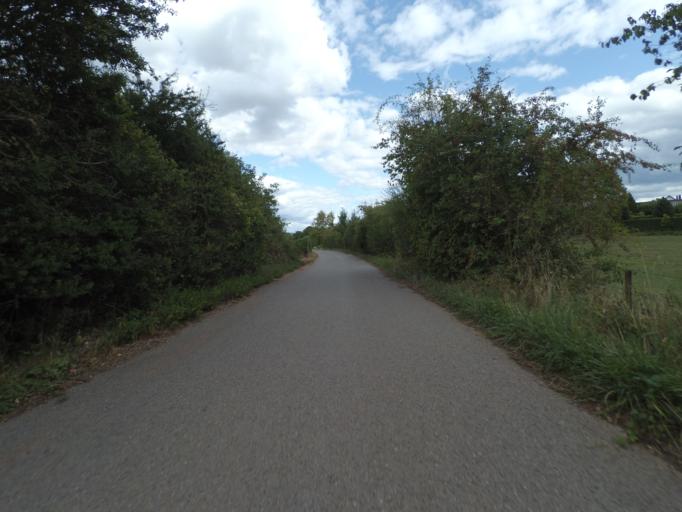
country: LU
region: Grevenmacher
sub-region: Canton de Remich
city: Remich
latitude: 49.5430
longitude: 6.3534
